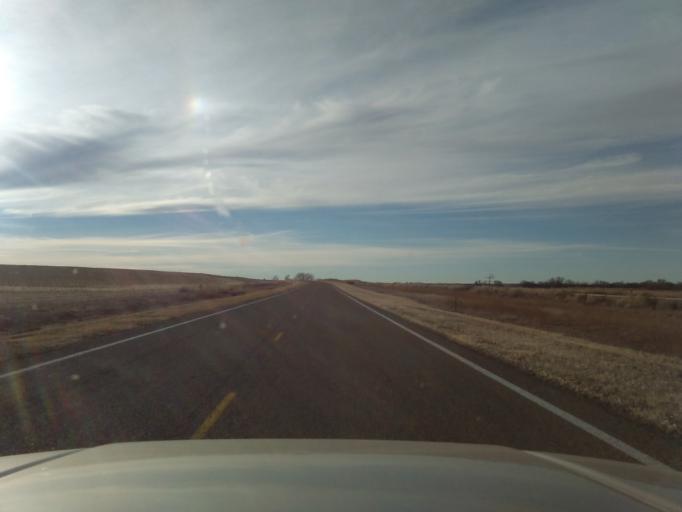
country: US
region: Kansas
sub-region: Norton County
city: Norton
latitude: 39.7523
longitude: -100.1373
